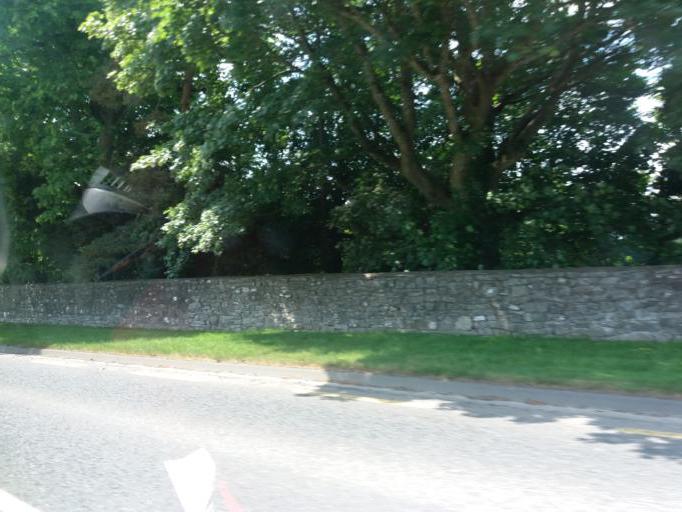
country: IE
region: Leinster
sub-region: An Mhi
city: Slane
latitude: 53.6947
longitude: -6.6075
